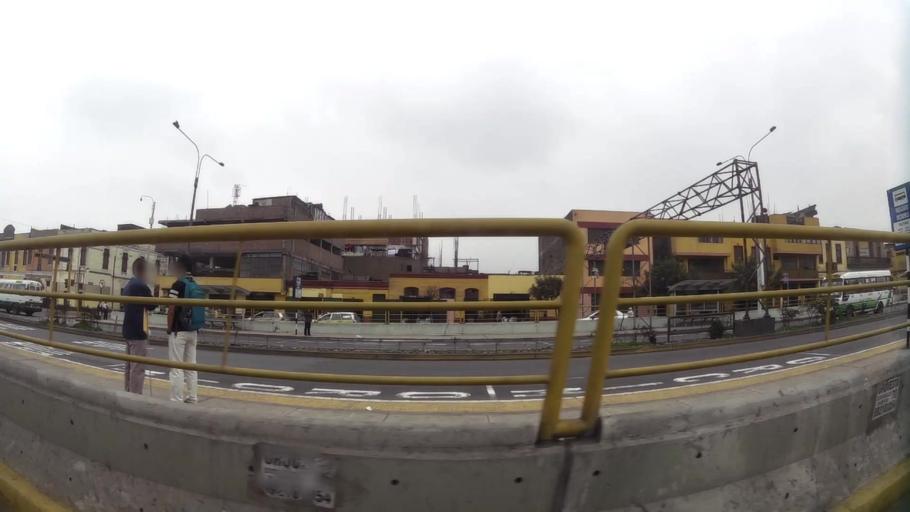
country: PE
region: Lima
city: Lima
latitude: -12.0576
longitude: -77.0189
